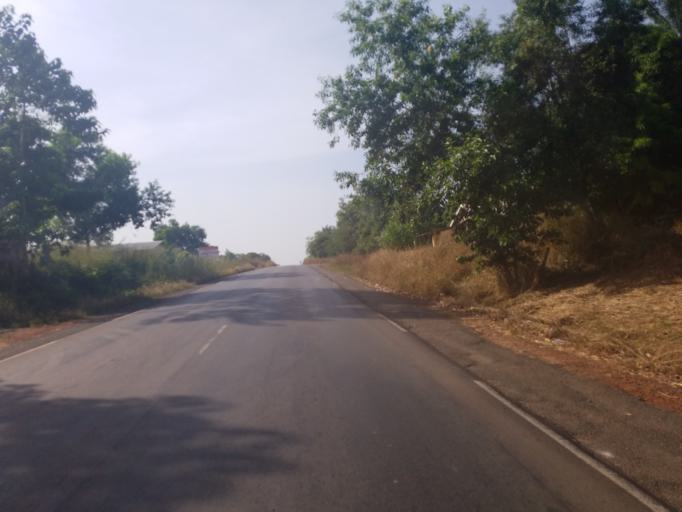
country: GN
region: Boke
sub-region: Boffa
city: Boffa
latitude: 10.1895
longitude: -14.0493
